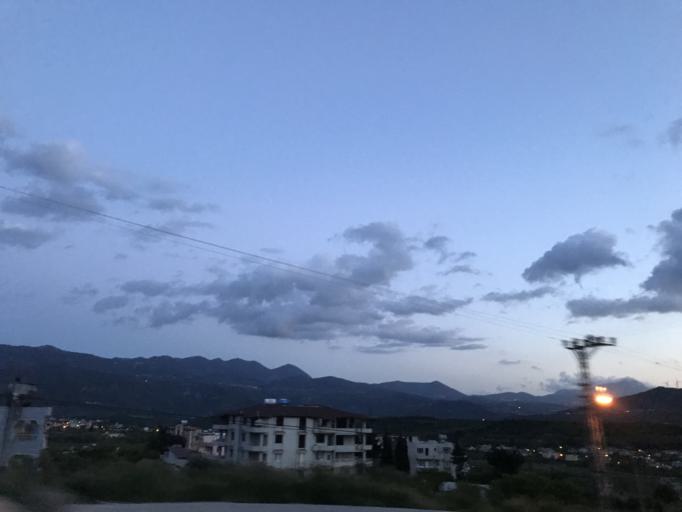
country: TR
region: Hatay
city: Karacay
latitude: 36.1455
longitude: 36.0752
